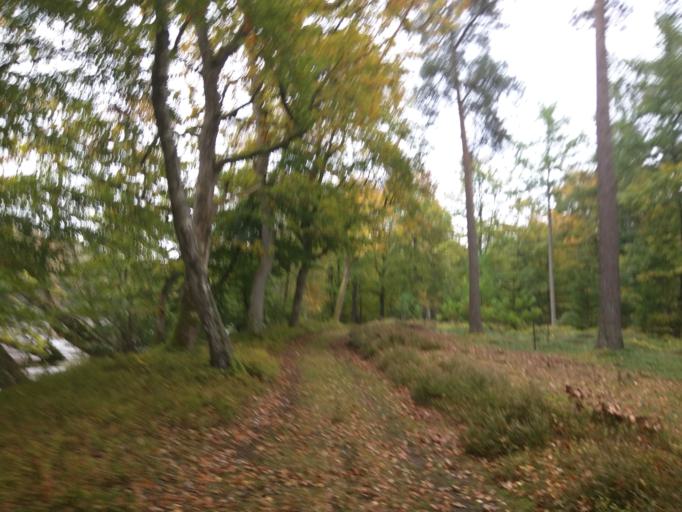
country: DK
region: Central Jutland
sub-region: Silkeborg Kommune
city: Virklund
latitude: 56.1522
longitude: 9.5693
